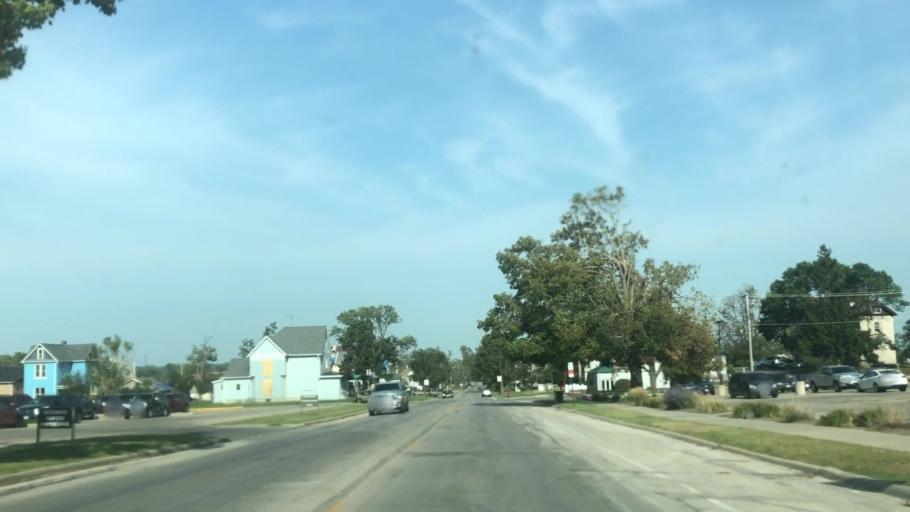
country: US
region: Iowa
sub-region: Marshall County
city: Marshalltown
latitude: 42.0491
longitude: -92.9060
